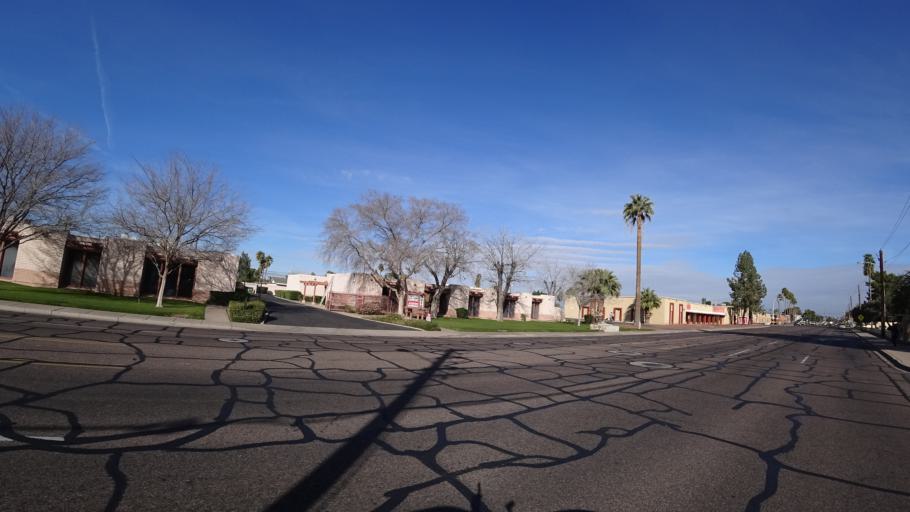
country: US
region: Arizona
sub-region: Maricopa County
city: Glendale
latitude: 33.5638
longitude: -112.1342
